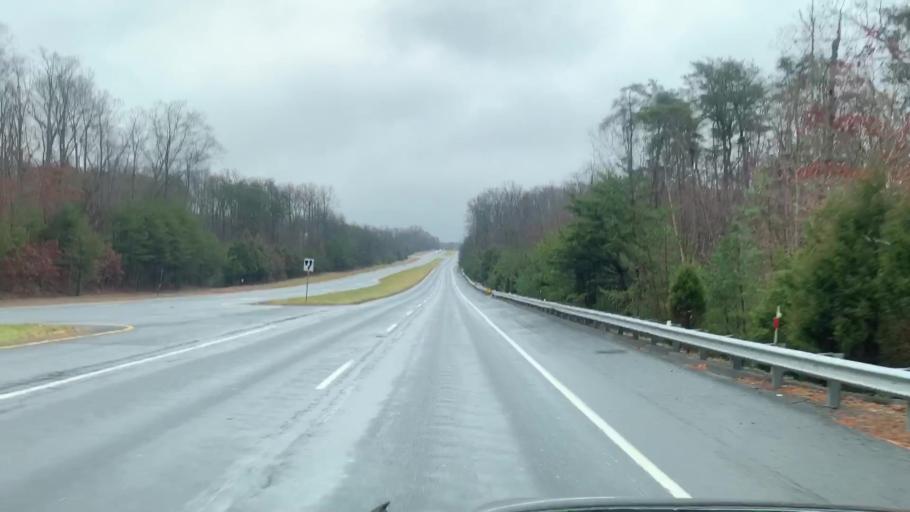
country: US
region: Virginia
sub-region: Fairfax County
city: Fairfax Station
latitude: 38.7736
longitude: -77.3219
